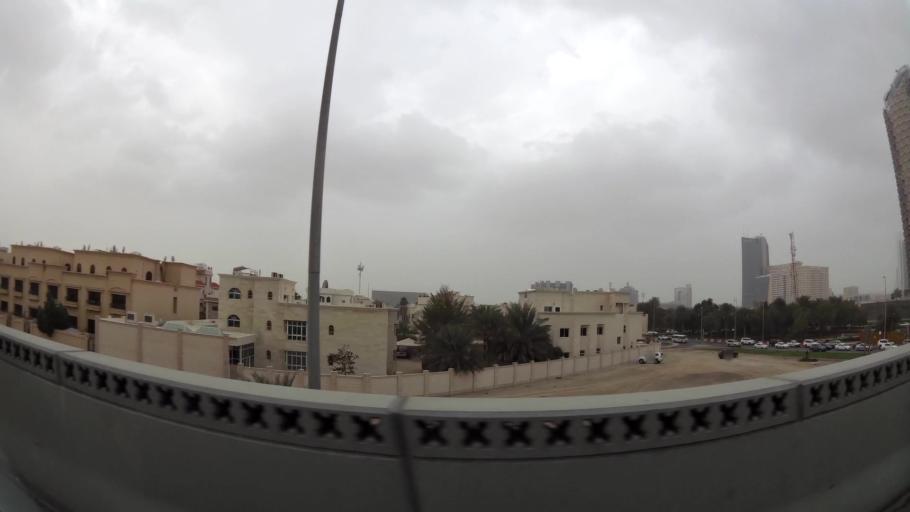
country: AE
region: Abu Dhabi
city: Abu Dhabi
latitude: 24.4547
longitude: 54.4037
